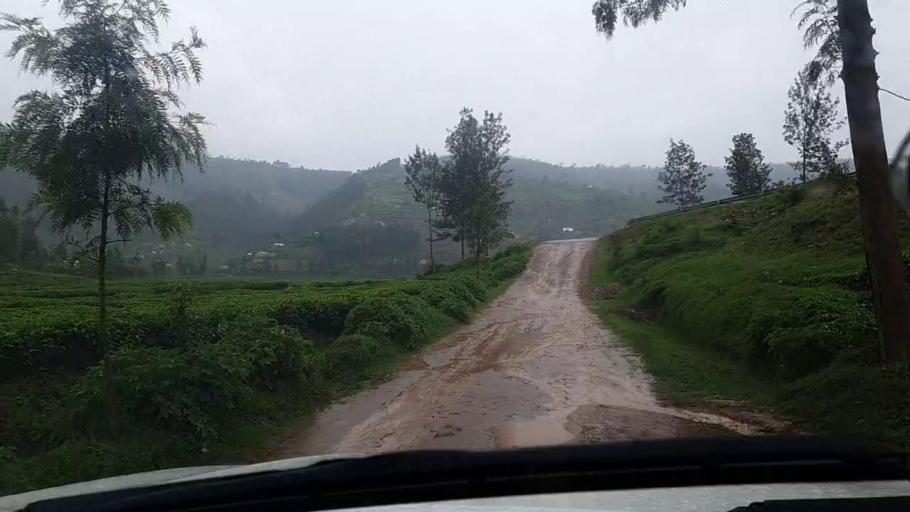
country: RW
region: Northern Province
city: Byumba
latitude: -1.6534
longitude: 29.9135
